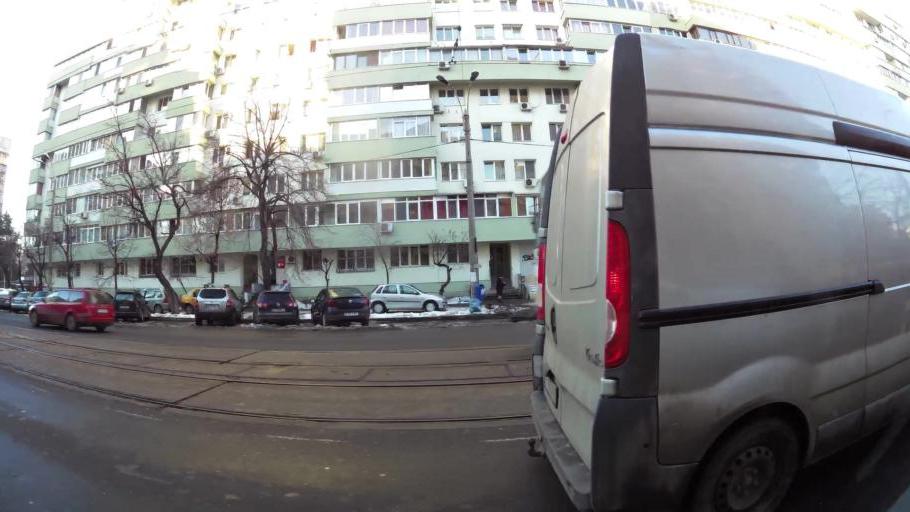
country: RO
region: Ilfov
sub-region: Comuna Fundeni-Dobroesti
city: Fundeni
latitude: 44.4438
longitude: 26.1482
